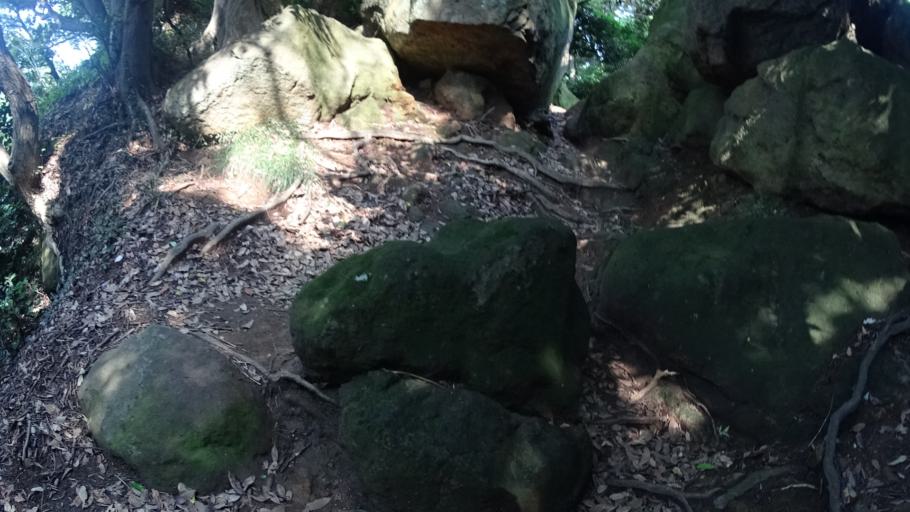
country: JP
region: Kanagawa
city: Zushi
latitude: 35.3062
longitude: 139.6105
